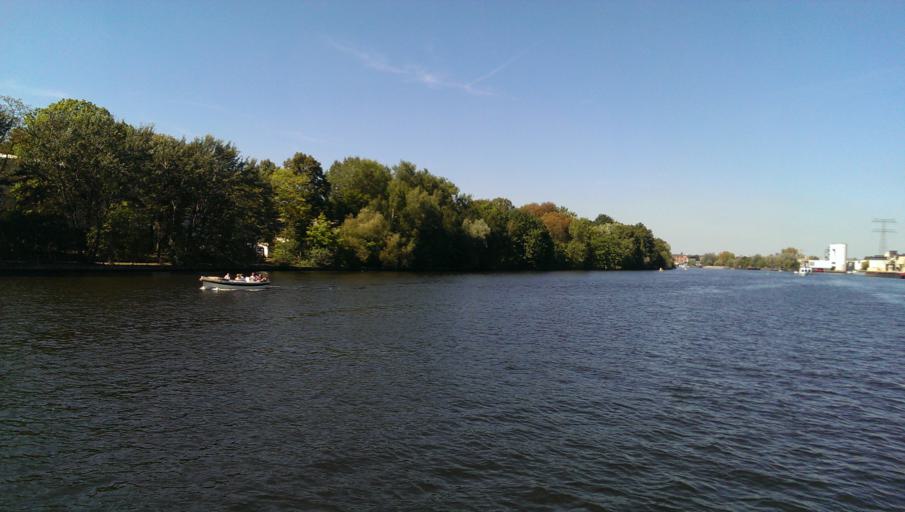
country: DE
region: Berlin
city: Baumschulenweg
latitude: 52.4813
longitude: 13.4961
